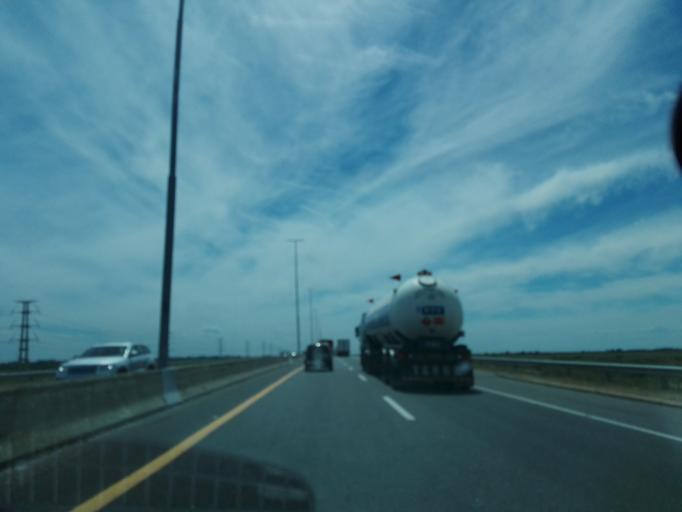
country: AR
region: Buenos Aires
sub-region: Partido de La Plata
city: La Plata
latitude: -34.8459
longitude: -58.0543
